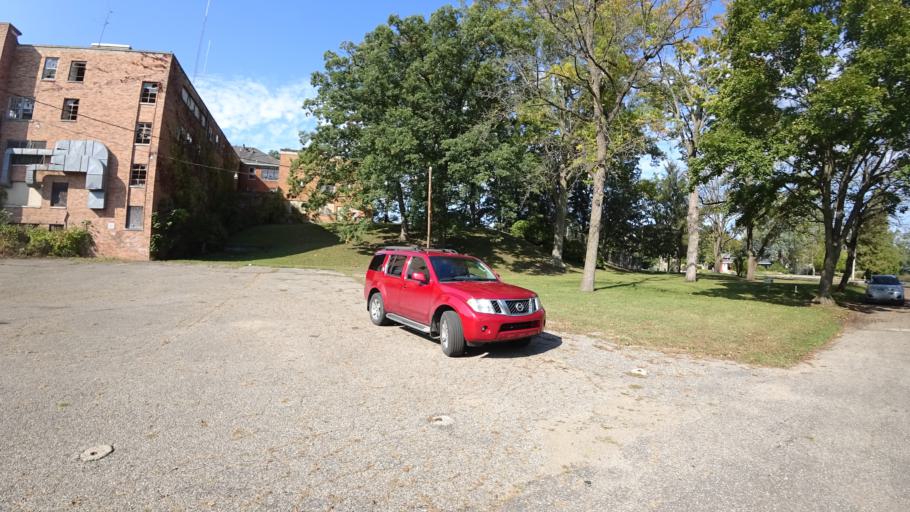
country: US
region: Michigan
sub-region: Saint Joseph County
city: Three Rivers
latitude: 41.9408
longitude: -85.6341
